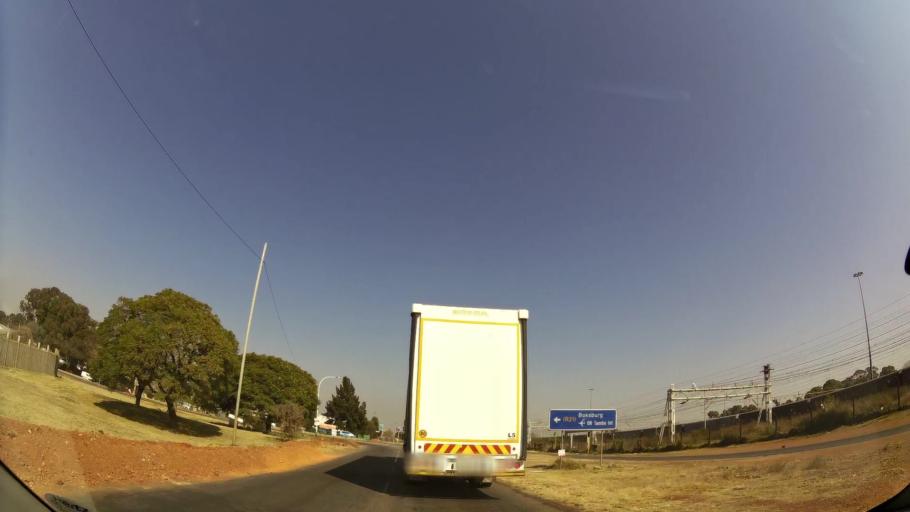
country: ZA
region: Gauteng
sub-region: Ekurhuleni Metropolitan Municipality
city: Boksburg
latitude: -26.1522
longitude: 28.2153
